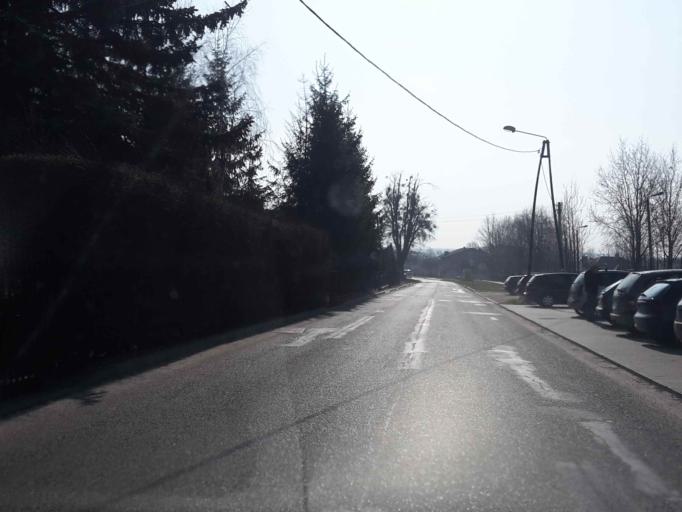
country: PL
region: Kujawsko-Pomorskie
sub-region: Powiat brodnicki
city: Brodnica
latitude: 53.2748
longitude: 19.4100
